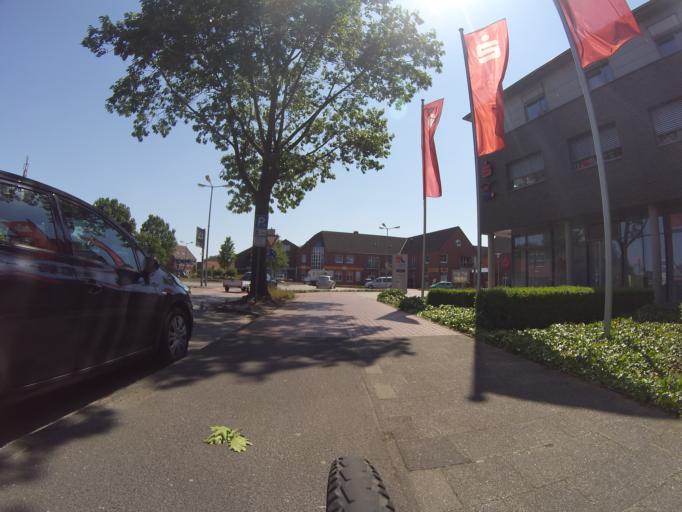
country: DE
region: Lower Saxony
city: Emlichheim
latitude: 52.6074
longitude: 6.8533
